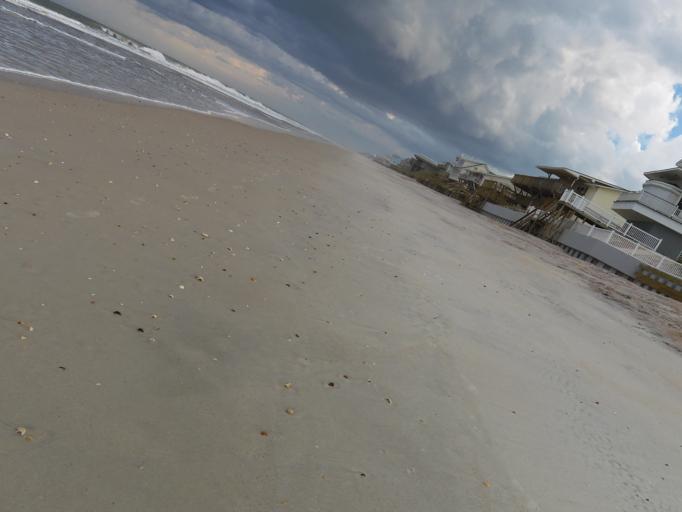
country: US
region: Florida
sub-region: Saint Johns County
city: Villano Beach
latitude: 29.9601
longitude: -81.3064
